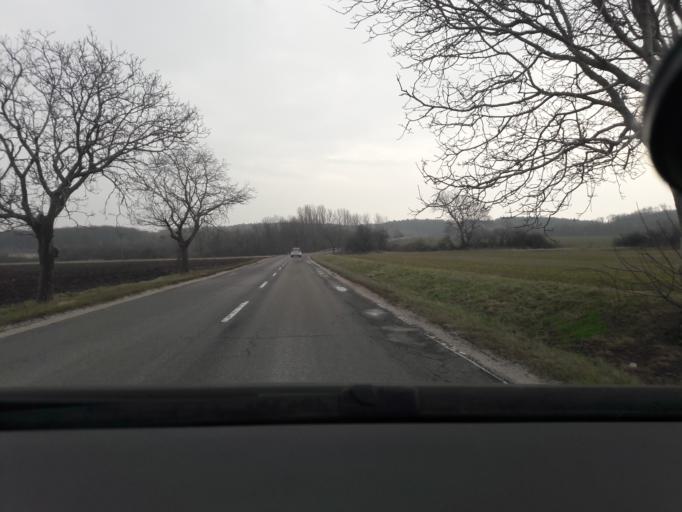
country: SK
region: Trnavsky
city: Smolenice
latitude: 48.4869
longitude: 17.4262
